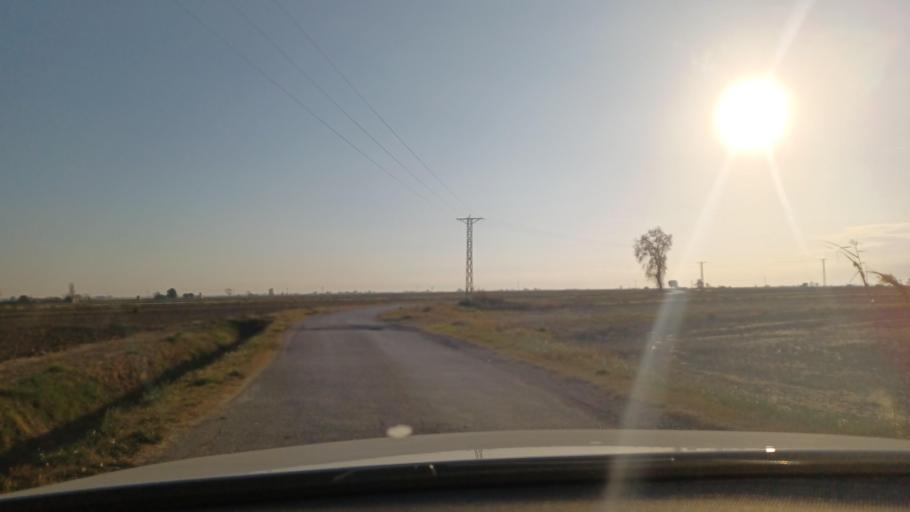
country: ES
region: Catalonia
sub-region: Provincia de Tarragona
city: Amposta
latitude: 40.7033
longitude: 0.6359
